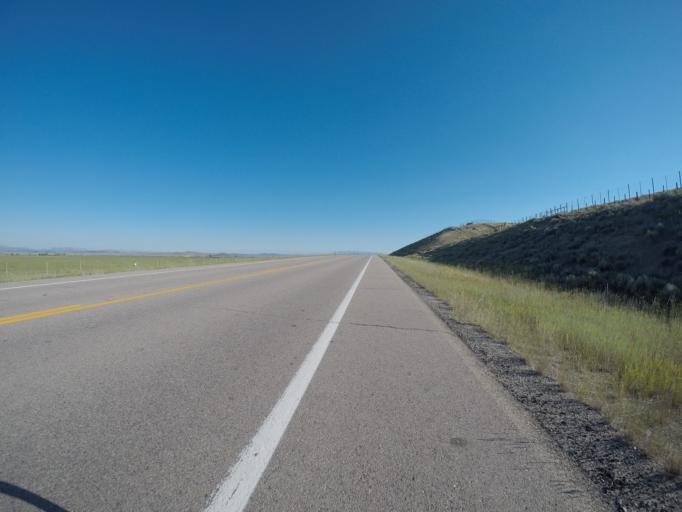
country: US
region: Wyoming
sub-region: Sublette County
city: Pinedale
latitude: 42.9429
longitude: -110.0835
